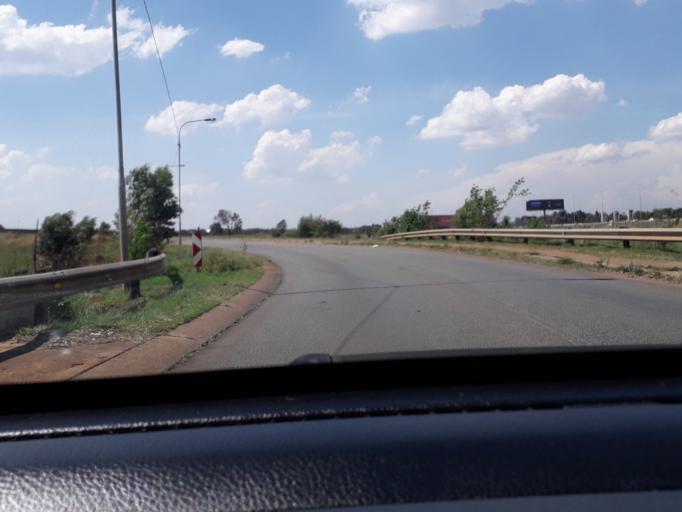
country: ZA
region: Gauteng
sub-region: City of Tshwane Metropolitan Municipality
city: Centurion
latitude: -25.8496
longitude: 28.2264
